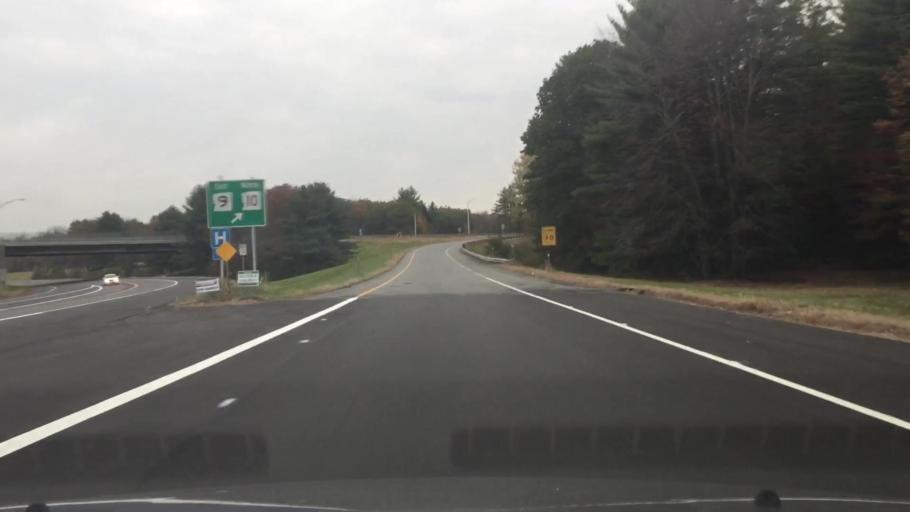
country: US
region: New Hampshire
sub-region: Cheshire County
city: Keene
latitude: 42.9424
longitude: -72.2951
